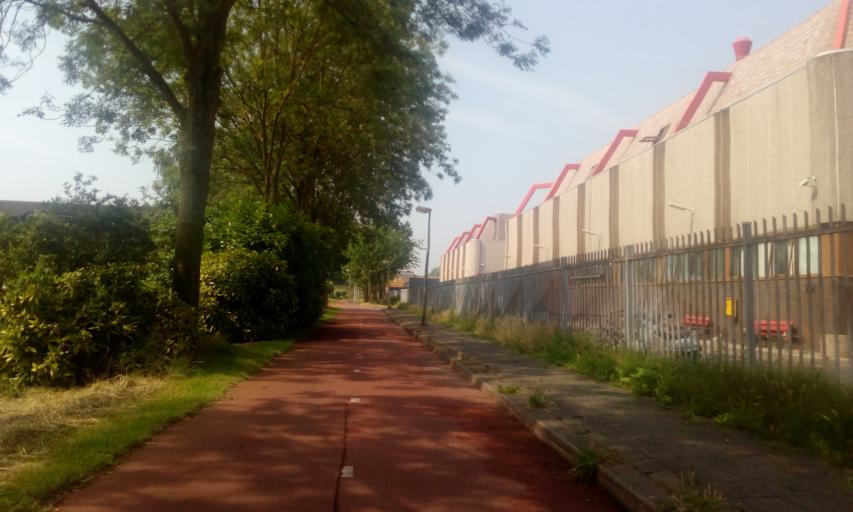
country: NL
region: South Holland
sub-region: Gemeente Capelle aan den IJssel
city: Capelle aan den IJssel
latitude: 51.9550
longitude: 4.5761
